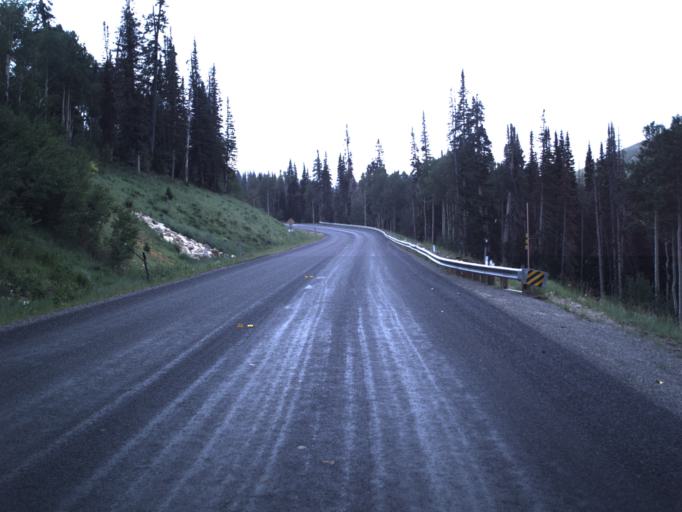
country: US
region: Utah
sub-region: Summit County
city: Francis
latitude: 40.4955
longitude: -111.0348
